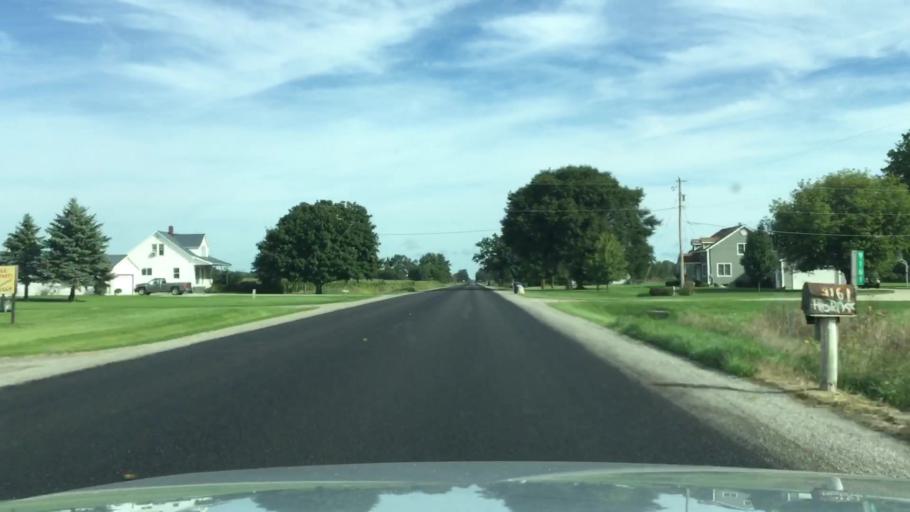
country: US
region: Michigan
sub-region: Genesee County
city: Montrose
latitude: 43.1373
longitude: -83.9292
